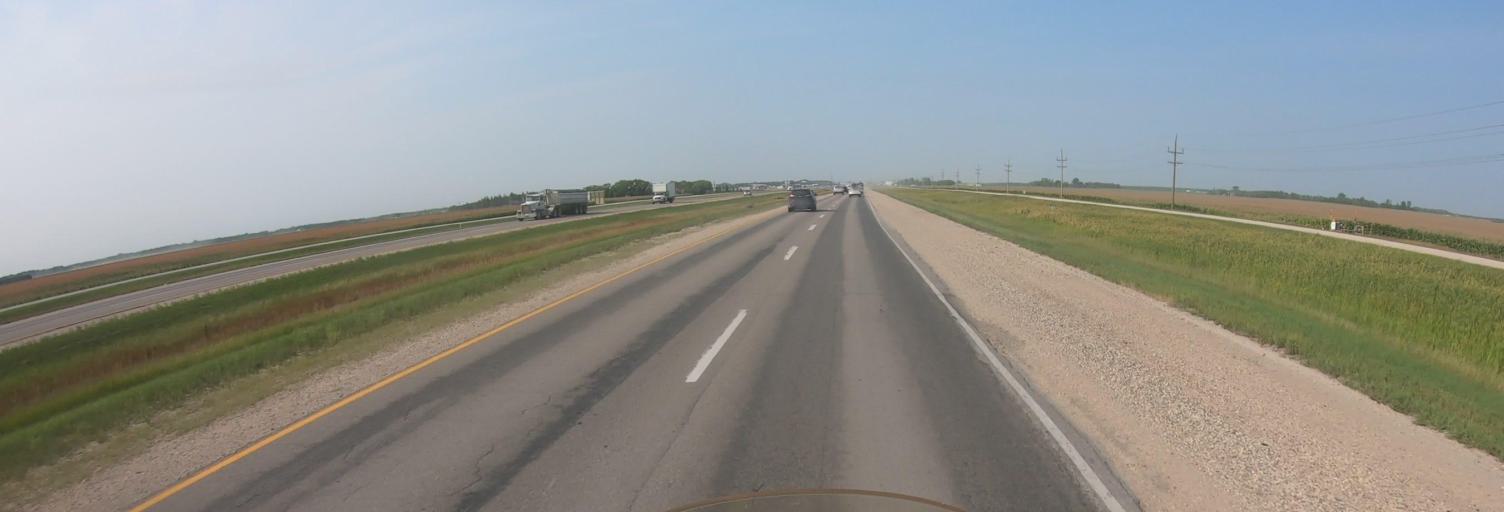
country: CA
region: Manitoba
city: Steinbach
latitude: 49.5835
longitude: -96.6874
